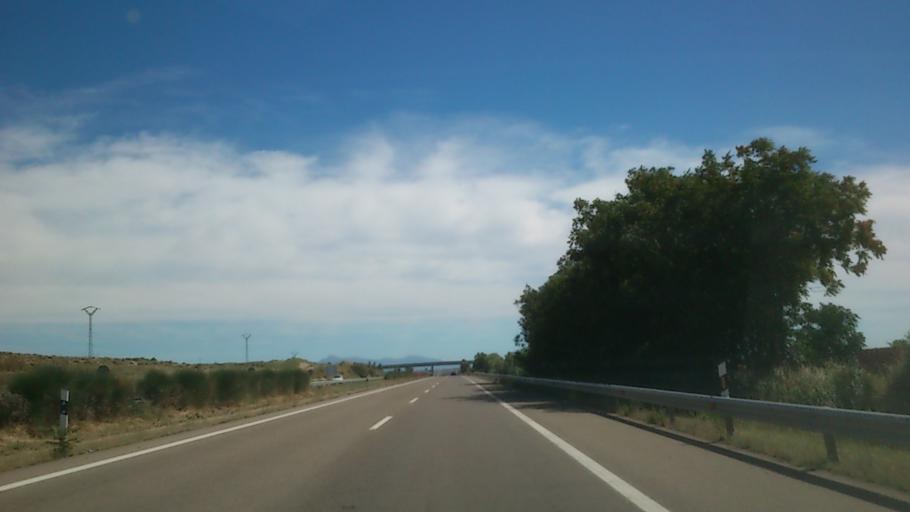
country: ES
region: Aragon
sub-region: Provincia de Huesca
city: Almudebar
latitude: 42.0196
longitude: -0.6106
